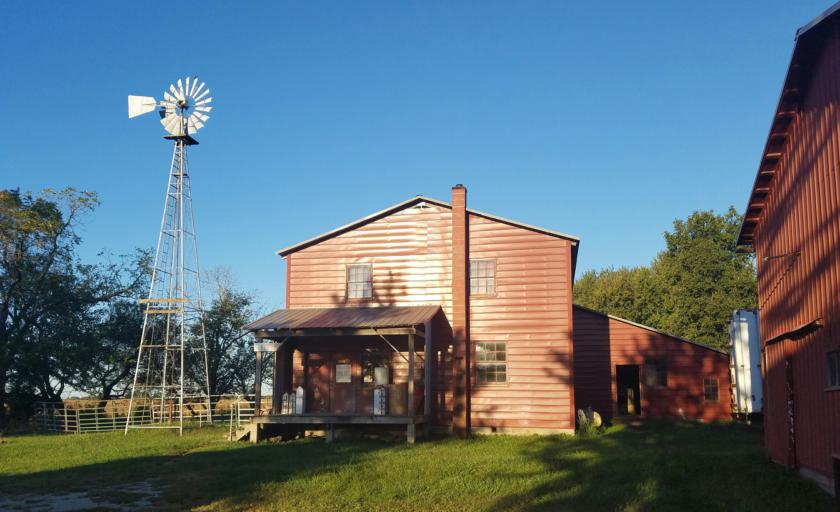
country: US
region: Iowa
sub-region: Decatur County
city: Lamoni
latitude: 40.5950
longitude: -93.9696
